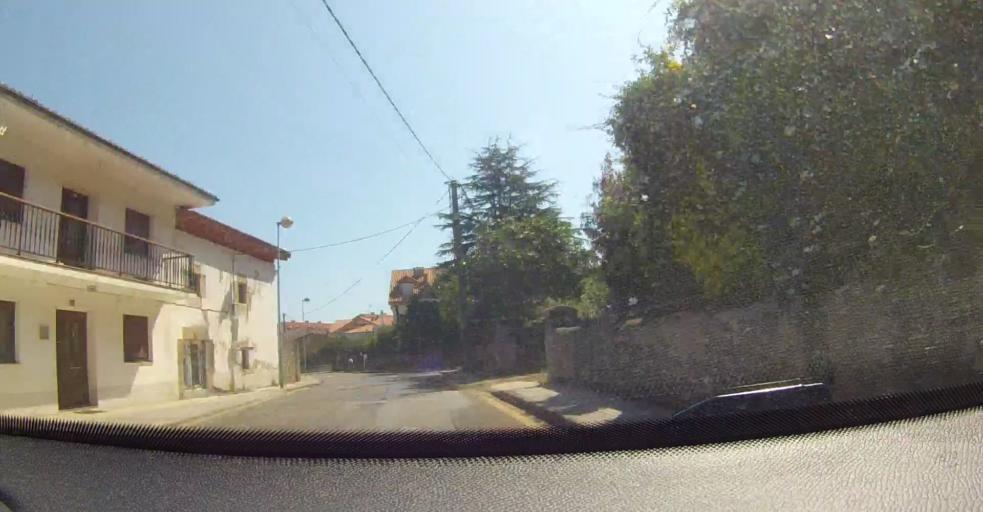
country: ES
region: Cantabria
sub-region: Provincia de Cantabria
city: Argonos
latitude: 43.4705
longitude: -3.5088
